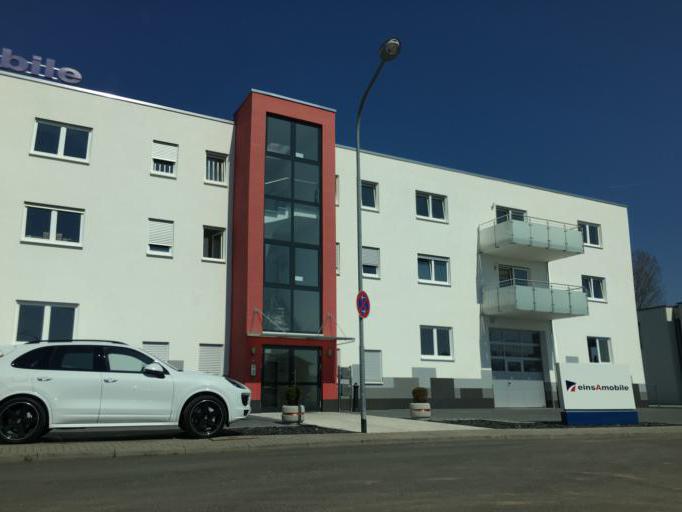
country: DE
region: Hesse
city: Obertshausen
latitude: 50.0769
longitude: 8.8756
